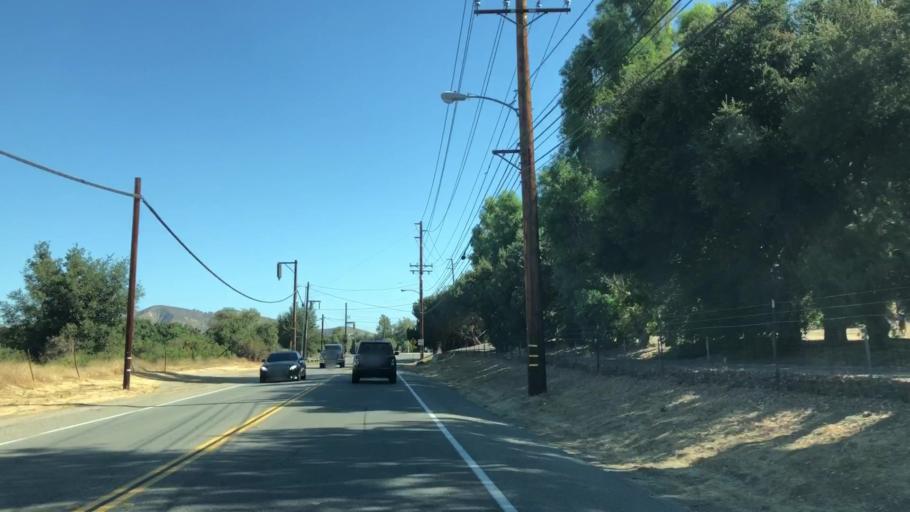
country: US
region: California
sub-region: Los Angeles County
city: Agoura
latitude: 34.1233
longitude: -118.7070
